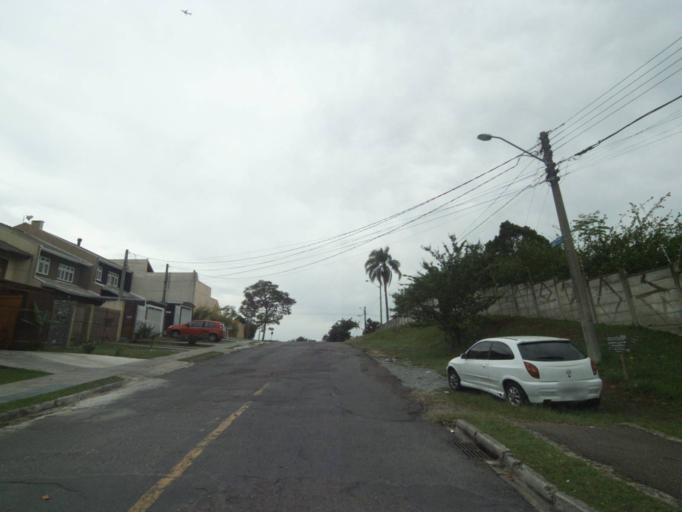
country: BR
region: Parana
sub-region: Pinhais
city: Pinhais
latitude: -25.4141
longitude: -49.2108
